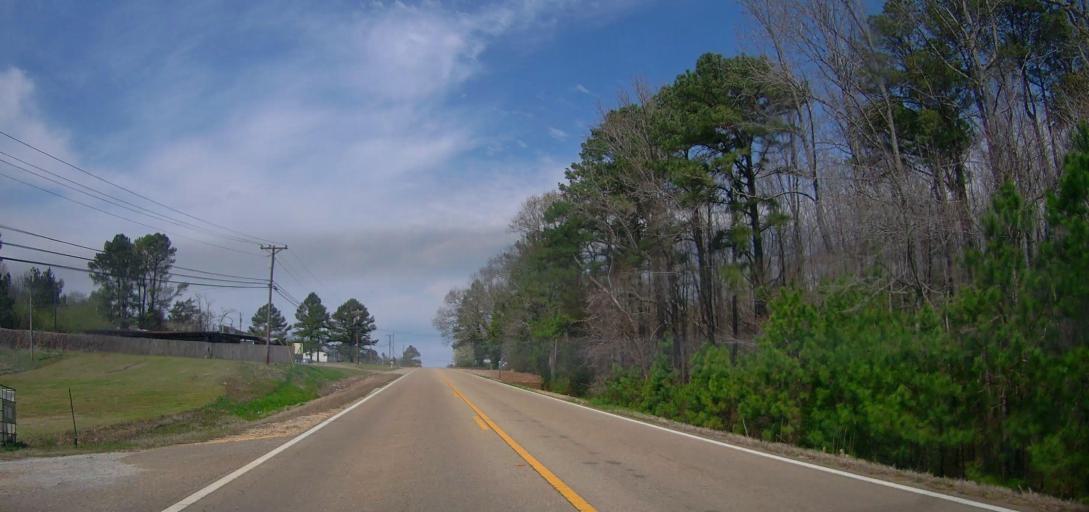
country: US
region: Mississippi
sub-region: Union County
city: New Albany
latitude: 34.4514
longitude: -88.9714
